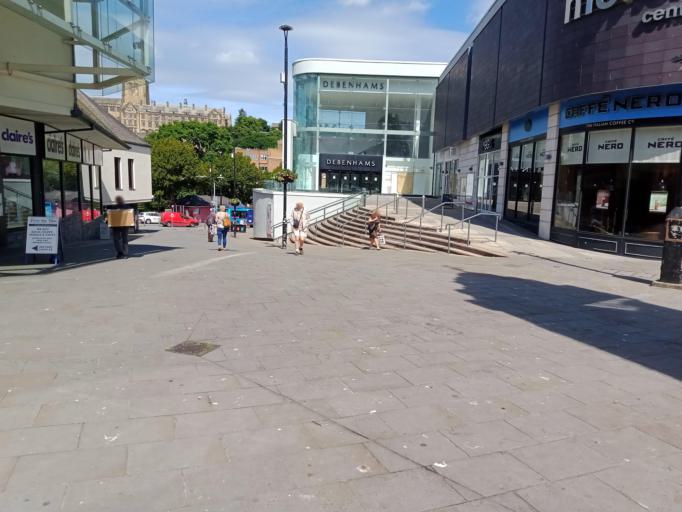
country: GB
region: Wales
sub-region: Gwynedd
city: Bangor
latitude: 53.2276
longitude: -4.1252
